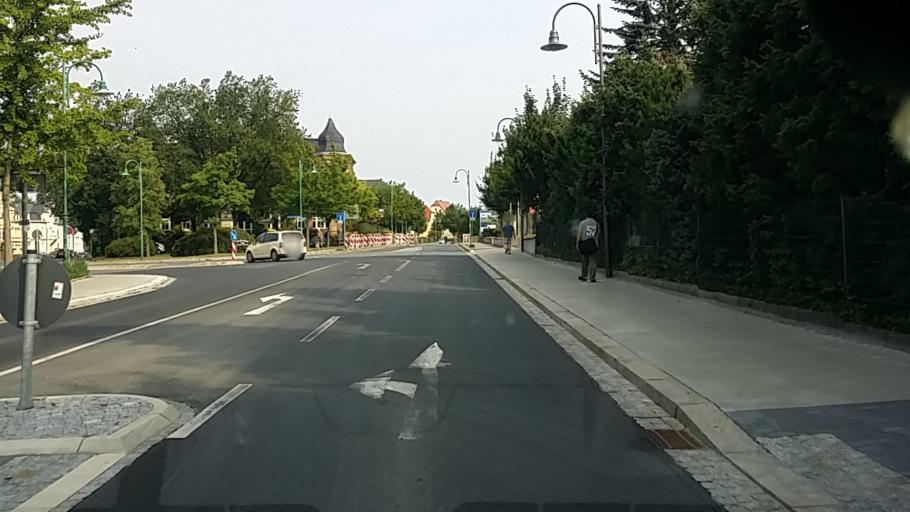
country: DE
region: Saxony
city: Radeberg
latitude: 51.1223
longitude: 13.9178
